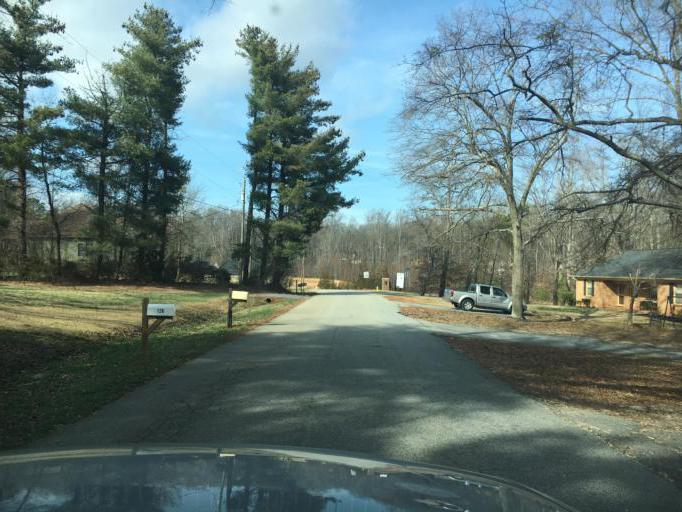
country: US
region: South Carolina
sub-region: Spartanburg County
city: Inman Mills
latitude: 35.0533
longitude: -82.1070
